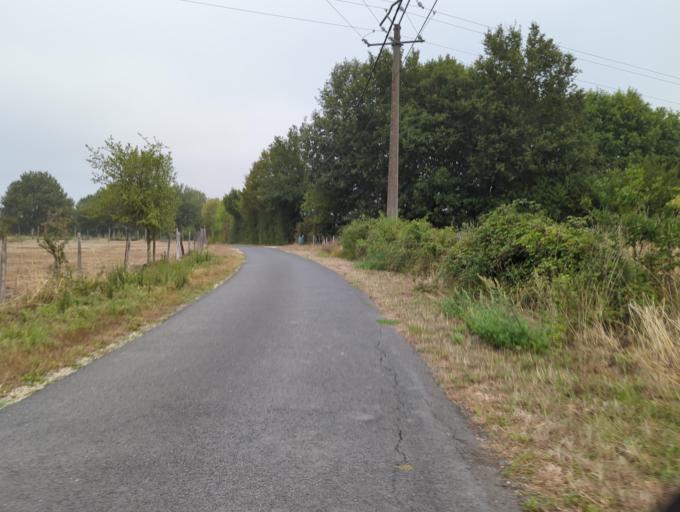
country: FR
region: Pays de la Loire
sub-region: Departement de Maine-et-Loire
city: Le Plessis-Grammoire
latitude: 47.4760
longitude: -0.4390
